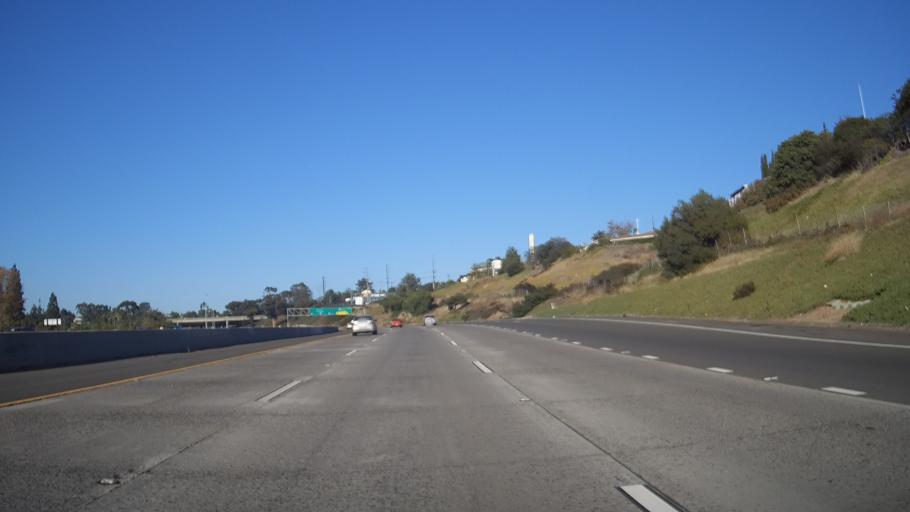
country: US
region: California
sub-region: San Diego County
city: San Diego
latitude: 32.7273
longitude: -117.1151
